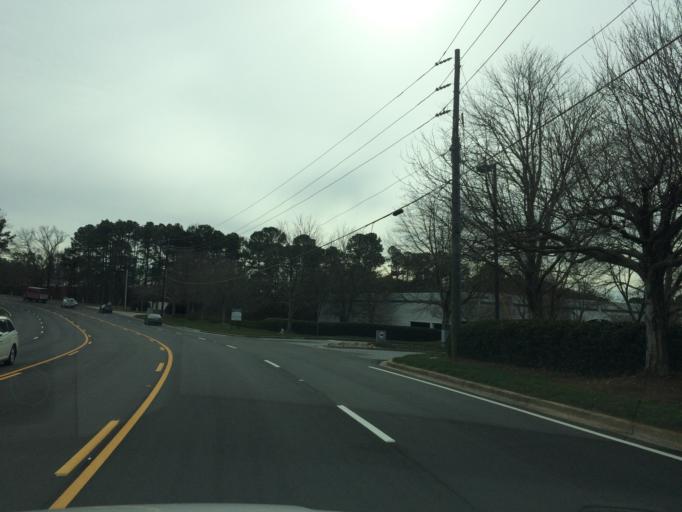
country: US
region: Georgia
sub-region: Gwinnett County
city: Duluth
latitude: 33.9757
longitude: -84.1011
